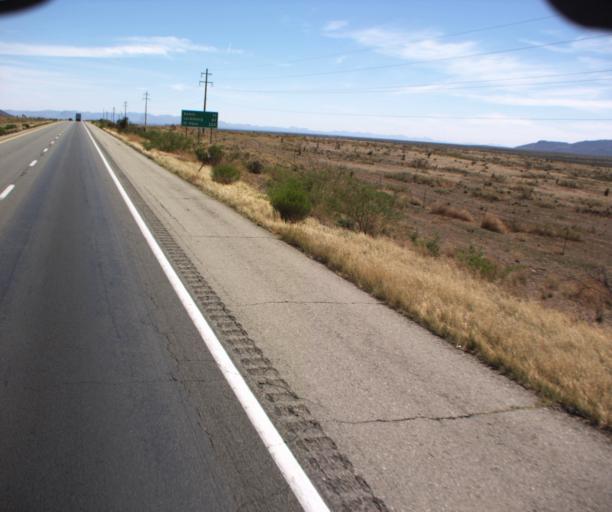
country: US
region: Arizona
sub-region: Cochise County
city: Willcox
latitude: 32.3612
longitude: -109.6588
